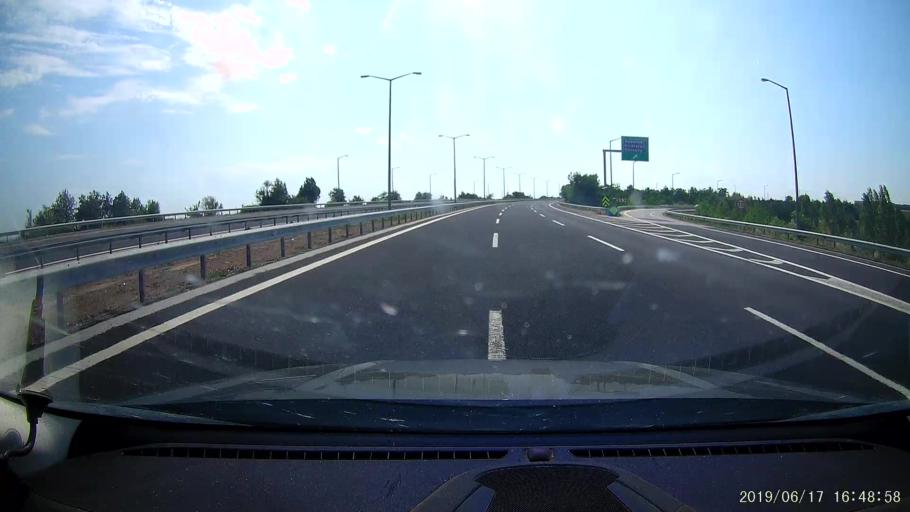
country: TR
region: Kirklareli
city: Babaeski
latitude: 41.5052
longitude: 27.1253
